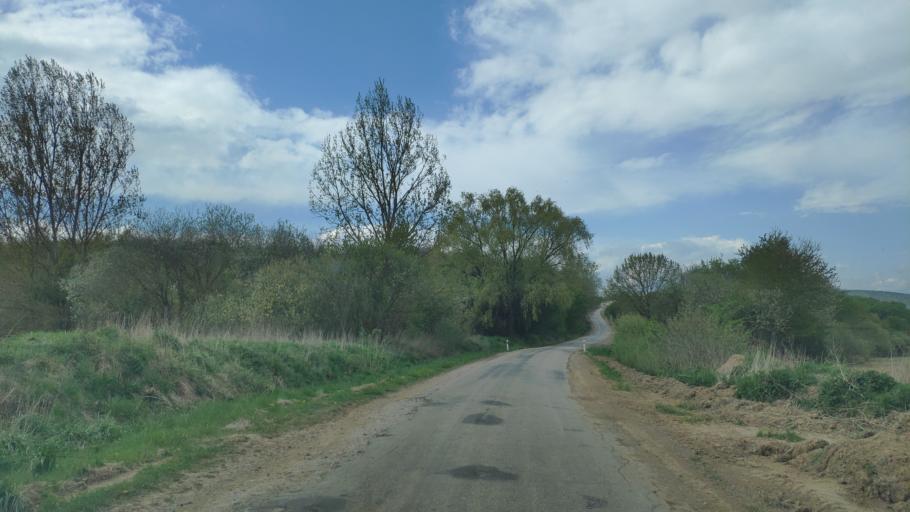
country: SK
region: Kosicky
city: Moldava nad Bodvou
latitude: 48.5751
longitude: 20.9308
